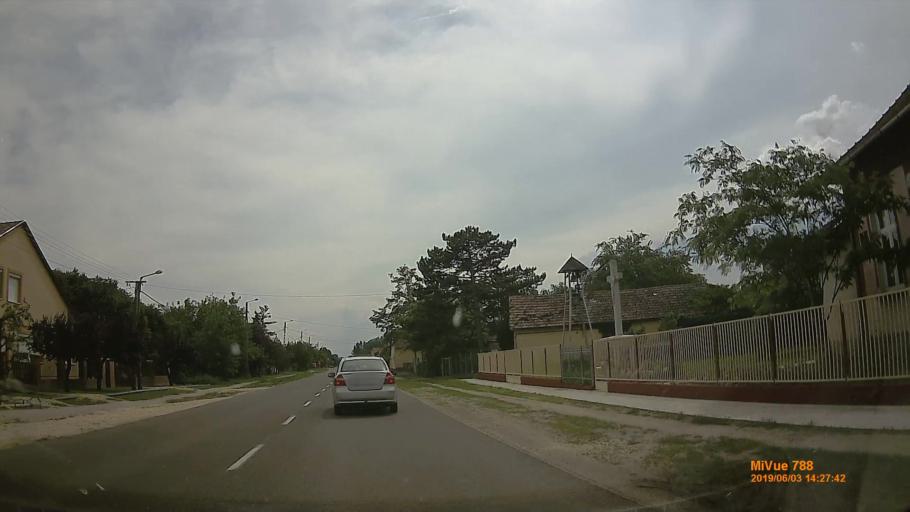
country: HU
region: Bacs-Kiskun
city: Tiszakecske
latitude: 46.9840
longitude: 20.1162
